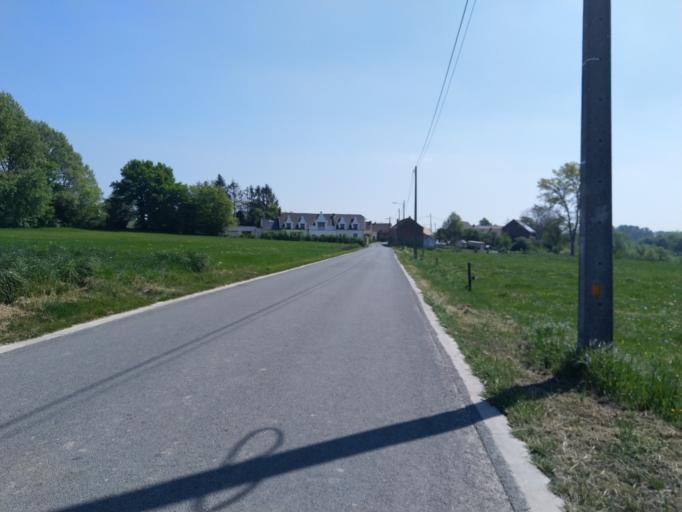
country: BE
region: Wallonia
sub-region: Province du Brabant Wallon
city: Rebecq-Rognon
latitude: 50.6398
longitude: 4.0733
